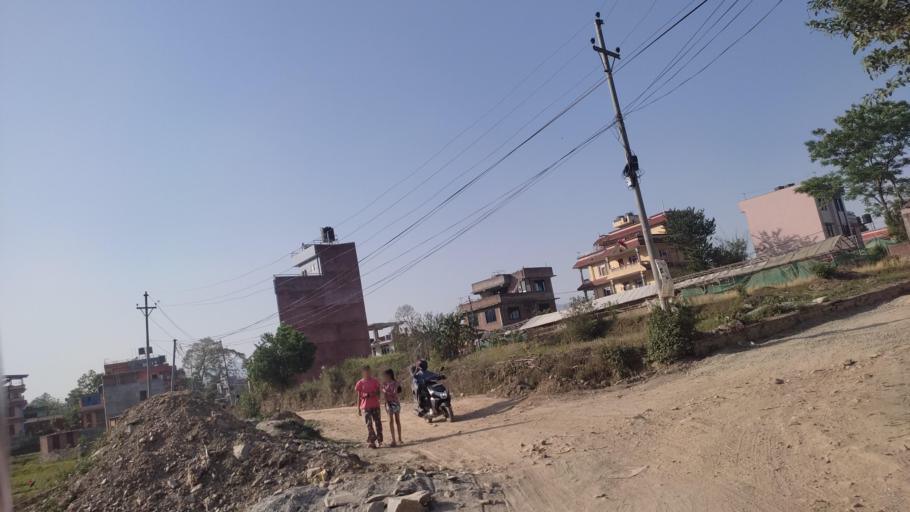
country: NP
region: Central Region
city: Kirtipur
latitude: 27.6535
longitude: 85.2751
